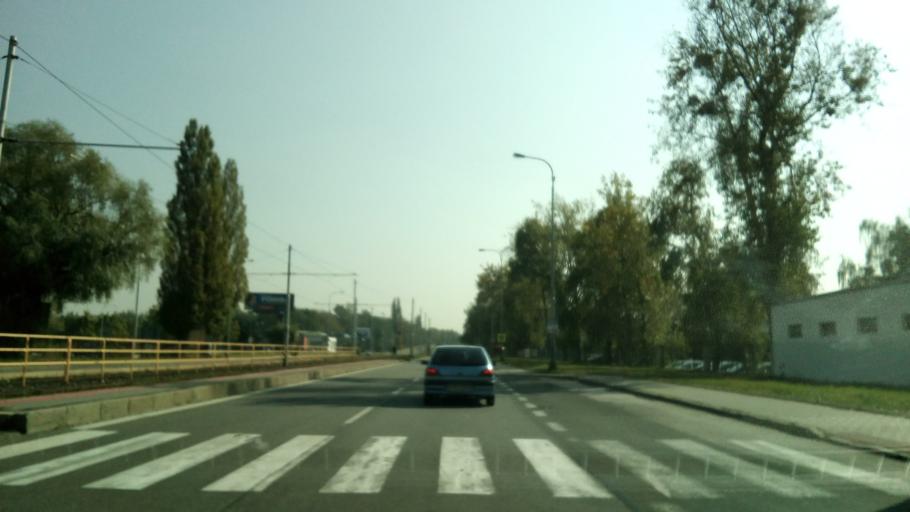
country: CZ
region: Moravskoslezsky
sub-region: Okres Ostrava-Mesto
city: Ostrava
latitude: 49.8145
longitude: 18.2390
